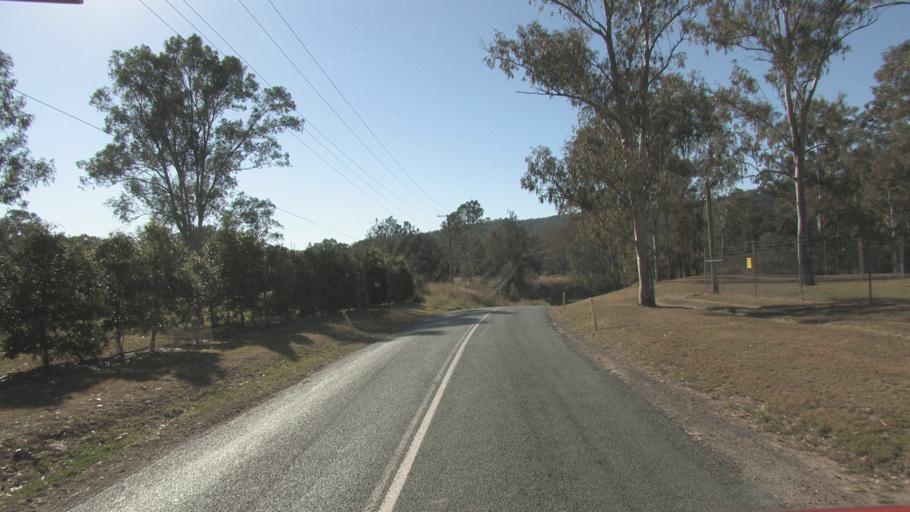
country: AU
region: Queensland
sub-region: Logan
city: Windaroo
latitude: -27.7962
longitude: 153.1758
